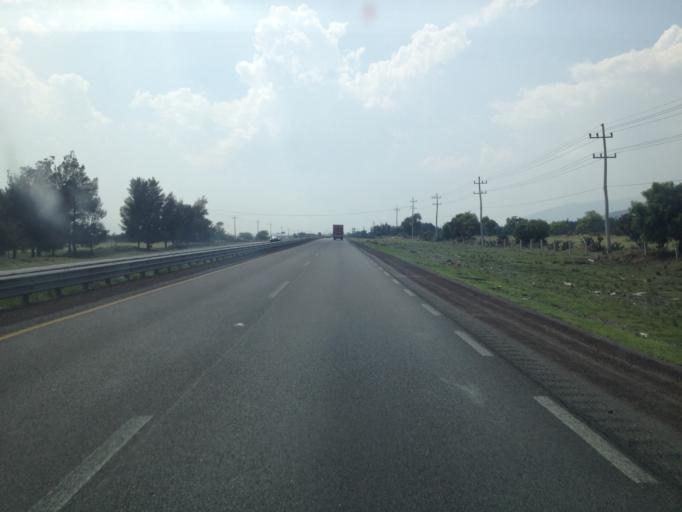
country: MX
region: Puebla
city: Cuacnopalan
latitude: 18.8353
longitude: -97.5141
